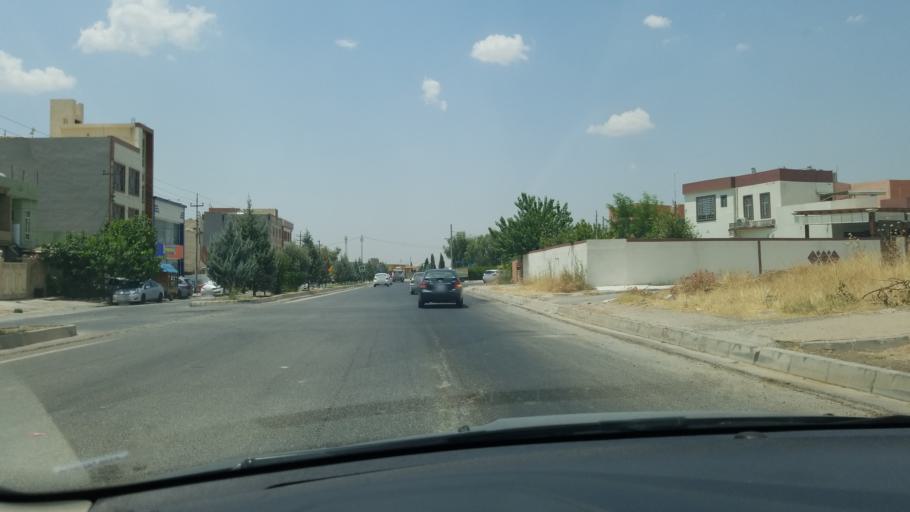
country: IQ
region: Arbil
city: Erbil
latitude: 36.1718
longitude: 44.0579
